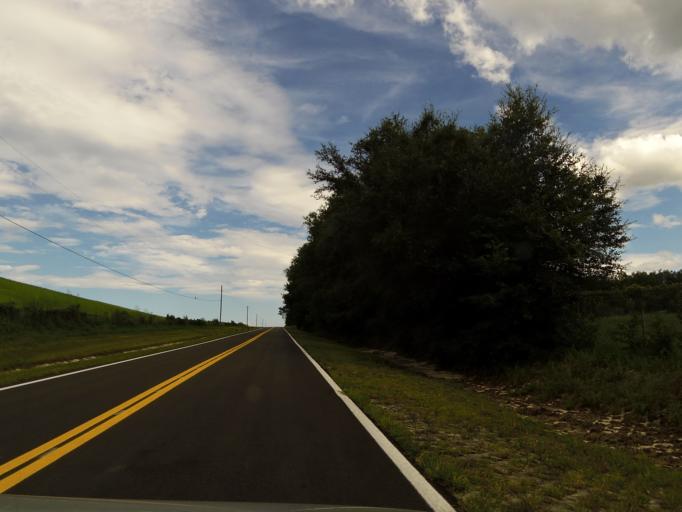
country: US
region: Florida
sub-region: Clay County
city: Green Cove Springs
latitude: 30.0066
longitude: -81.7467
